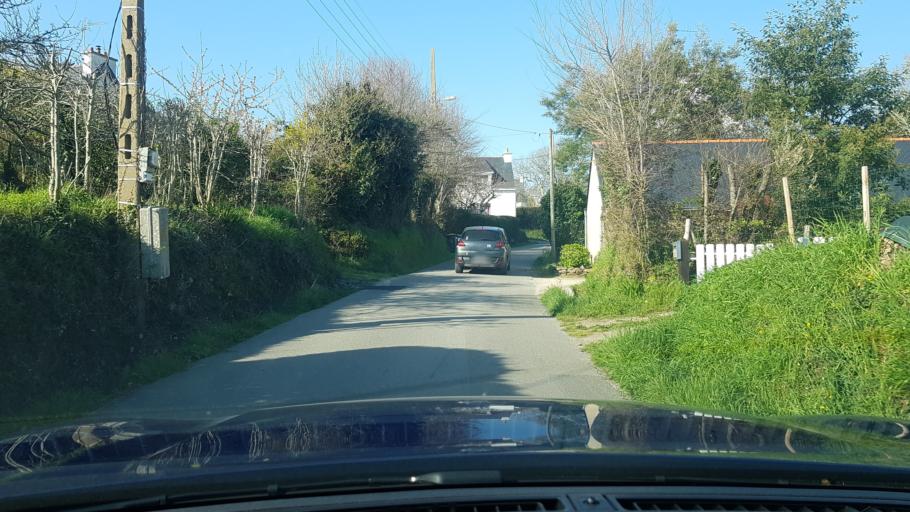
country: FR
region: Brittany
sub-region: Departement du Finistere
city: Moelan-sur-Mer
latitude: 47.7816
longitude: -3.6285
